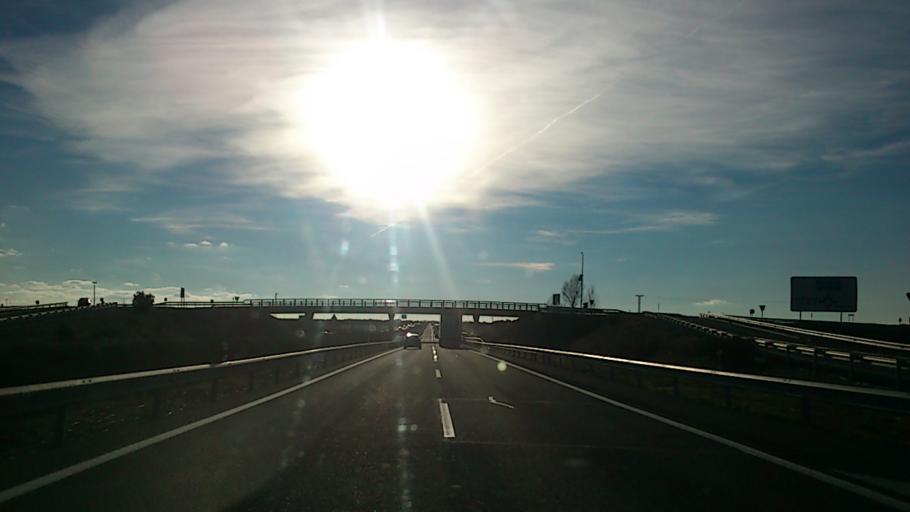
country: ES
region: Castille-La Mancha
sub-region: Provincia de Guadalajara
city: Mirabueno
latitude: 40.9312
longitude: -2.7127
